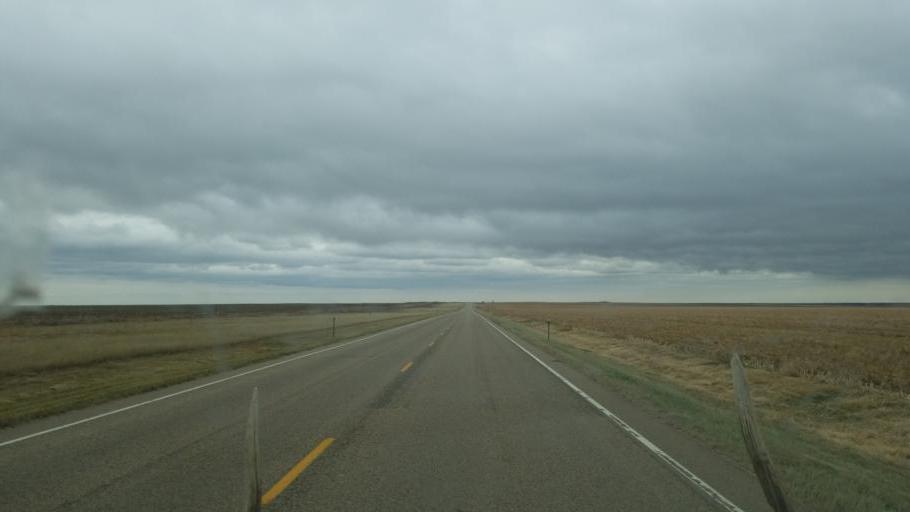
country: US
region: Colorado
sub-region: Cheyenne County
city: Cheyenne Wells
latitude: 38.8163
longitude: -102.5350
